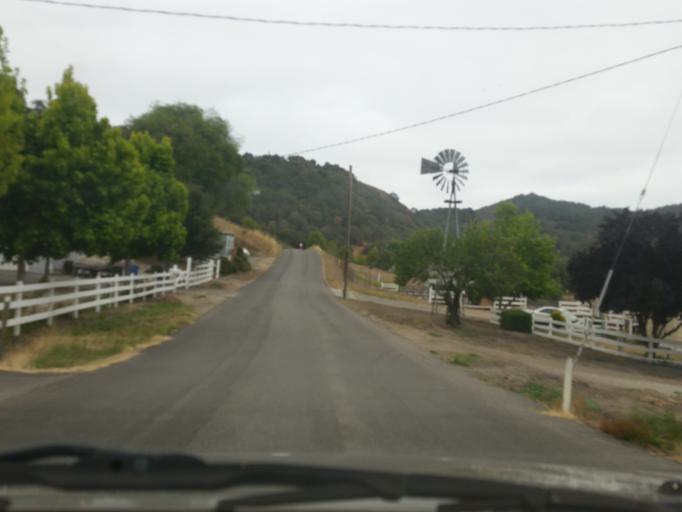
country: US
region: California
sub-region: San Luis Obispo County
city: Avila Beach
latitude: 35.1883
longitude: -120.6962
